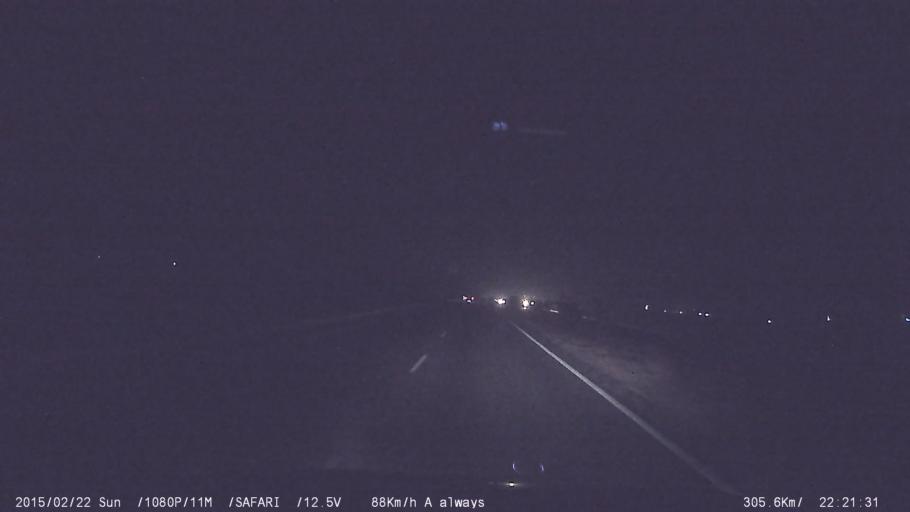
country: IN
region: Tamil Nadu
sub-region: Karur
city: Karur
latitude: 11.0035
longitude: 78.0679
